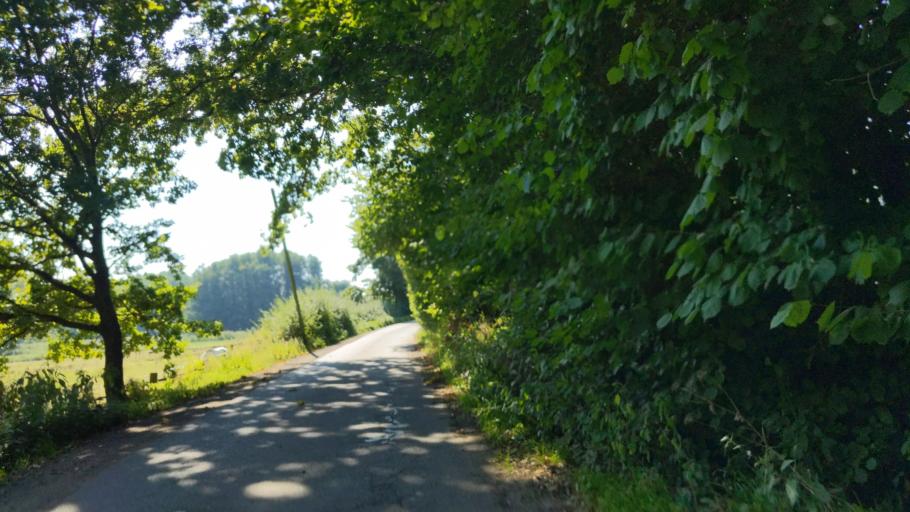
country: DE
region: Schleswig-Holstein
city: Heidekamp
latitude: 53.8475
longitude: 10.4898
